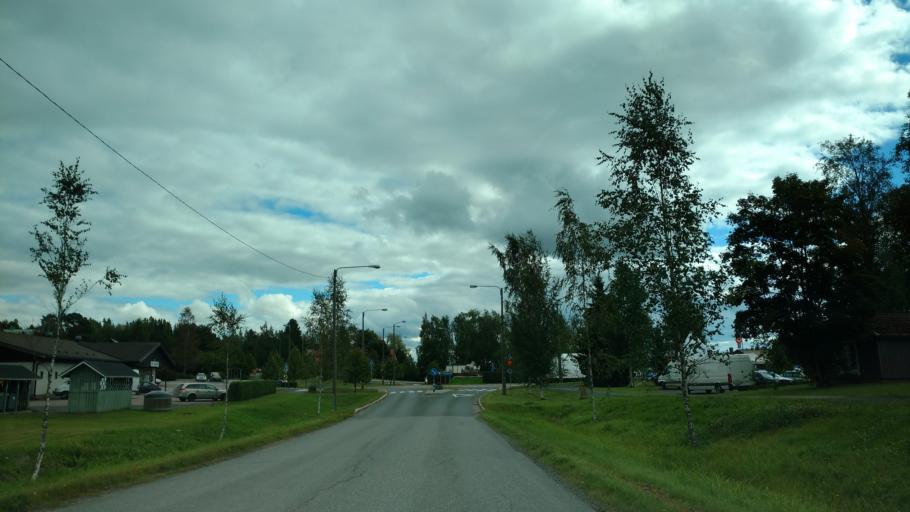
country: FI
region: Haeme
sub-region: Forssa
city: Ypaejae
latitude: 60.8047
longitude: 23.2809
